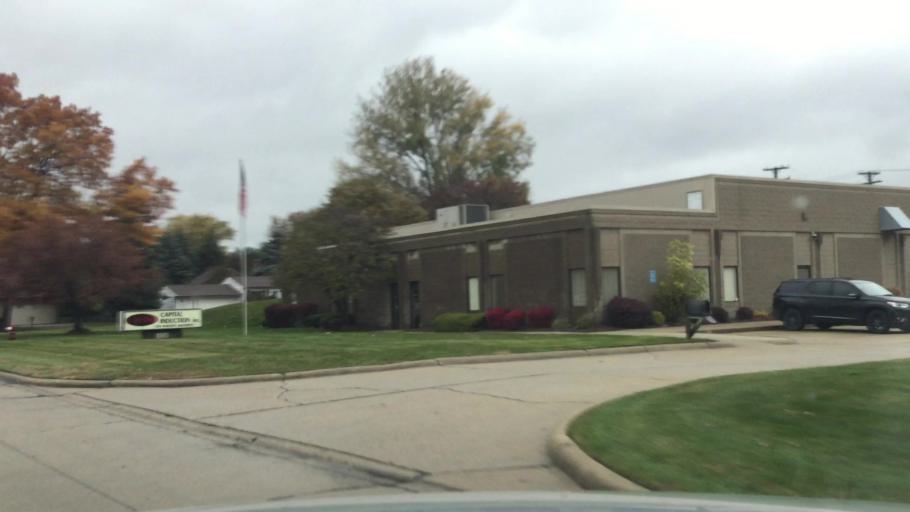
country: US
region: Michigan
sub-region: Macomb County
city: Utica
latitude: 42.6212
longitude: -83.0460
